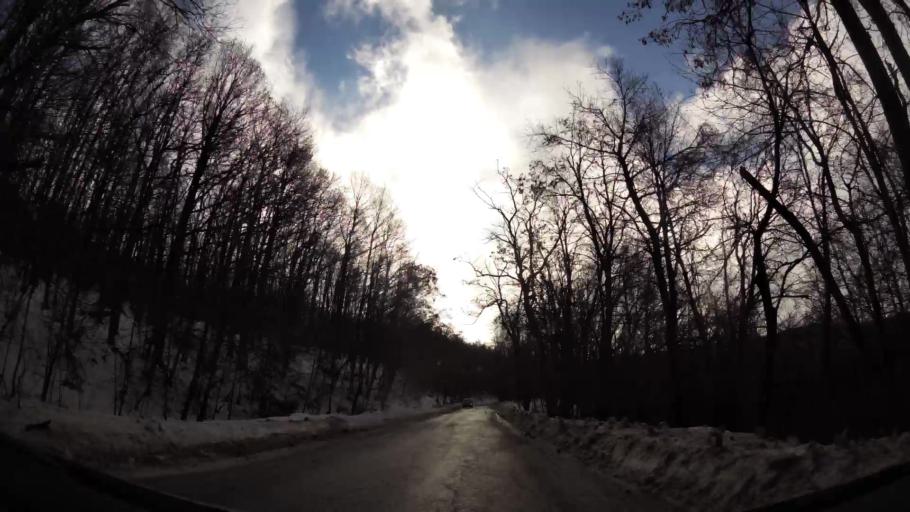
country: BG
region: Sofiya
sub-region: Obshtina Bozhurishte
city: Bozhurishte
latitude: 42.6369
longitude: 23.2216
